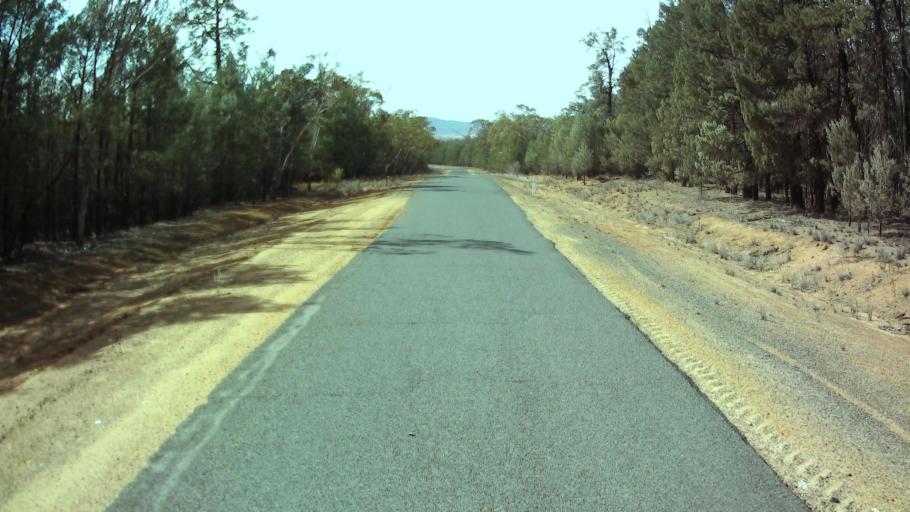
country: AU
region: New South Wales
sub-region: Weddin
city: Grenfell
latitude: -33.7454
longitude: 148.0545
